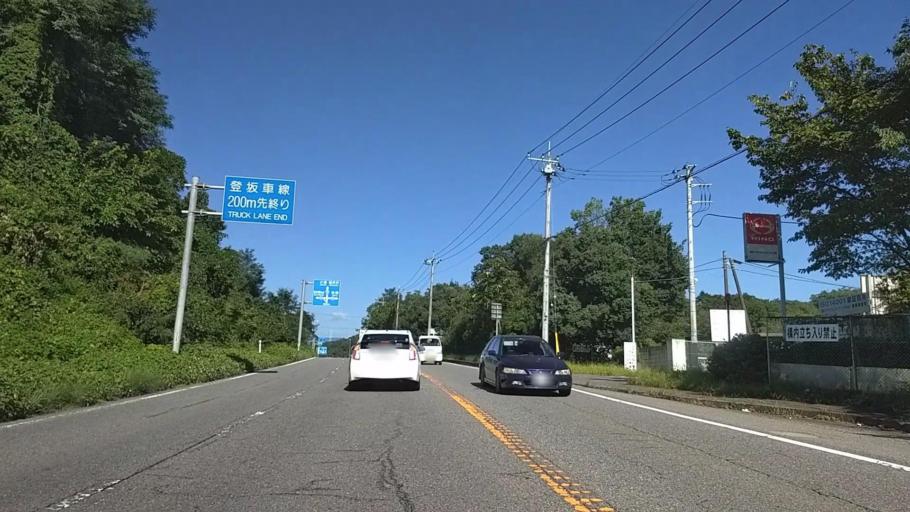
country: JP
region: Gunma
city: Annaka
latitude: 36.3125
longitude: 138.8119
